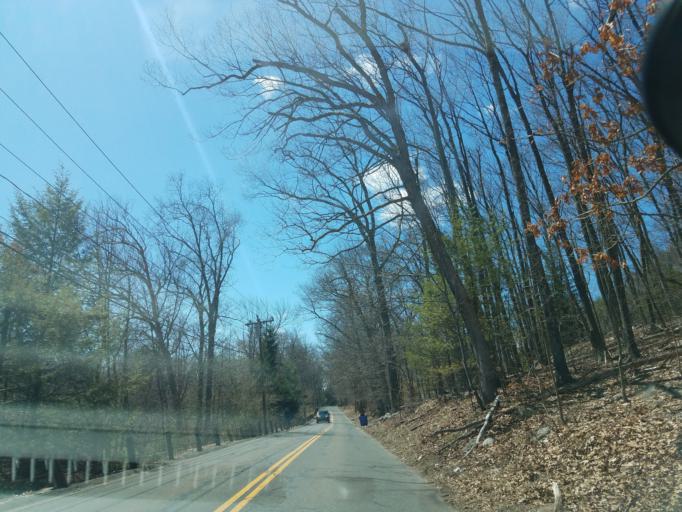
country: US
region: Connecticut
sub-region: Hartford County
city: Collinsville
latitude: 41.7827
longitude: -72.8979
